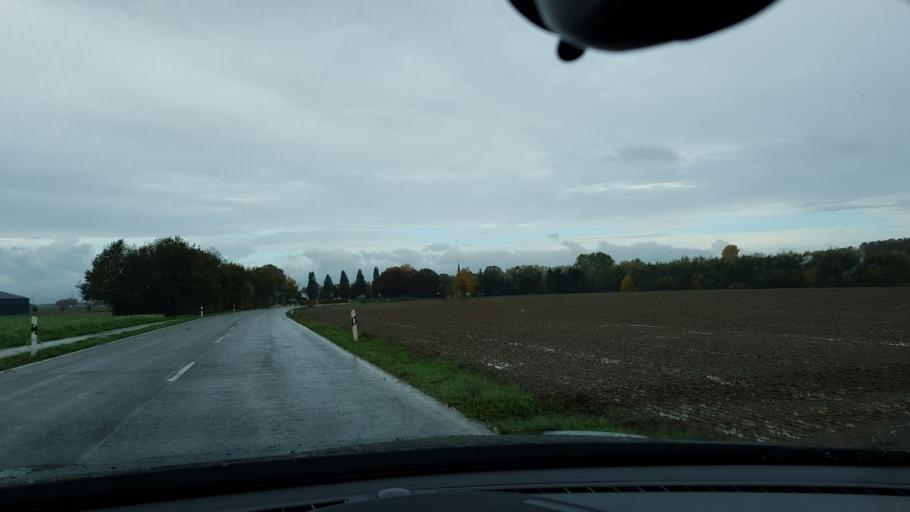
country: DE
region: North Rhine-Westphalia
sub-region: Regierungsbezirk Dusseldorf
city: Rommerskirchen
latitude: 51.0682
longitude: 6.7005
